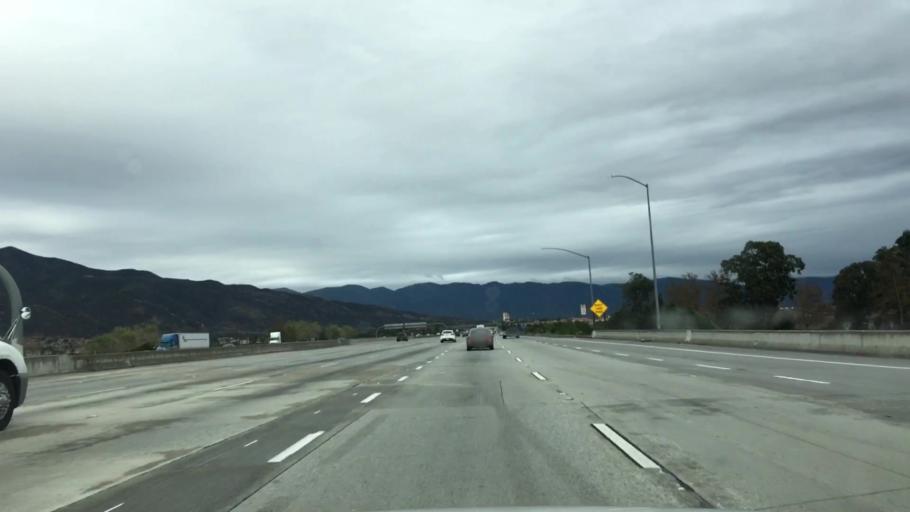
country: US
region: California
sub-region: San Bernardino County
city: Fontana
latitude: 34.1419
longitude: -117.4888
